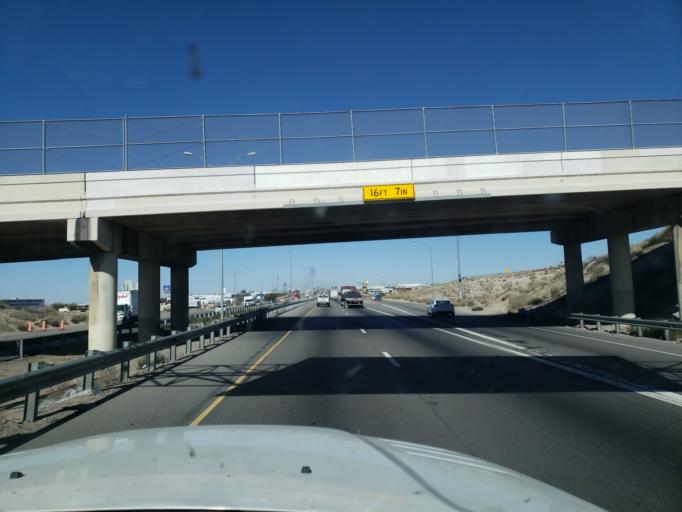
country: US
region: New Mexico
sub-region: Dona Ana County
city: Sunland Park
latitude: 31.8523
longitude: -106.5743
